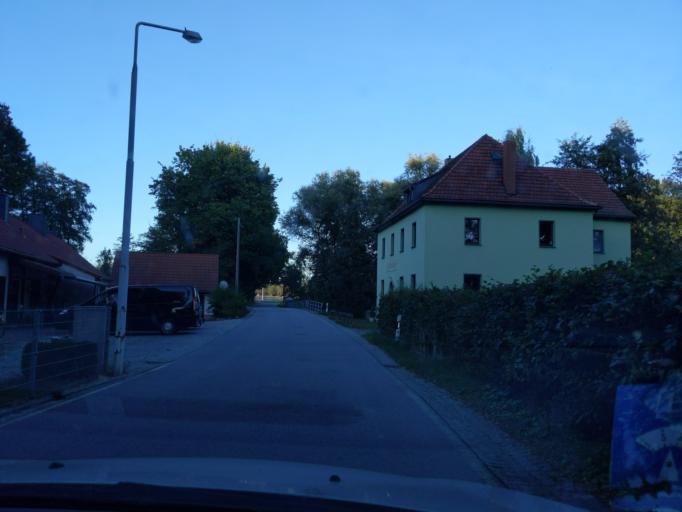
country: DE
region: Saxony
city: Guttau
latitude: 51.2716
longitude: 14.5697
